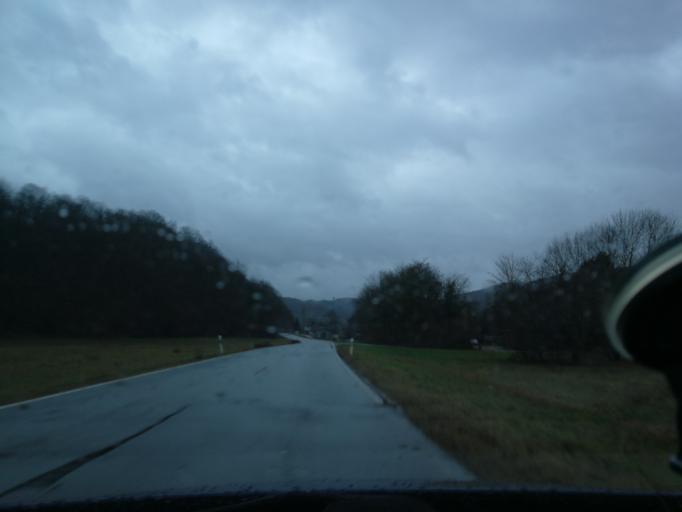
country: DE
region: Rheinland-Pfalz
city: Minheim
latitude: 49.8445
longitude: 6.9278
